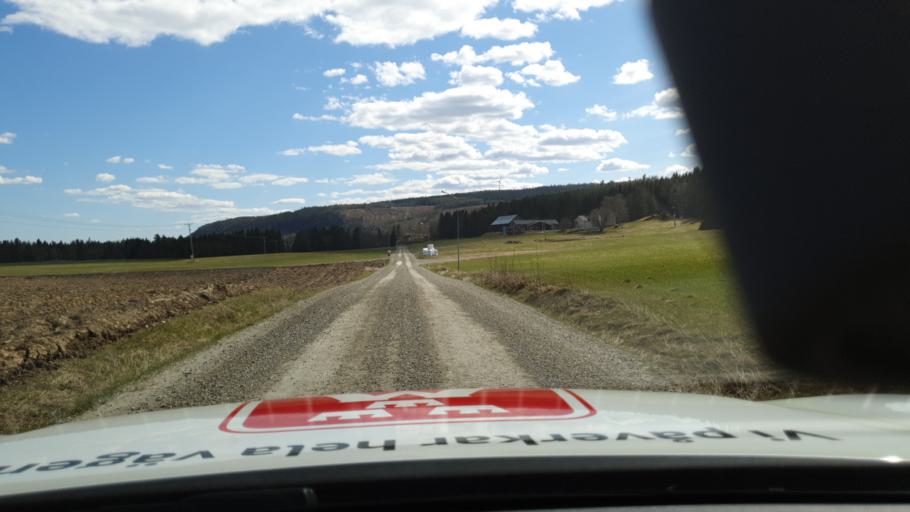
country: SE
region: Jaemtland
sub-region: Bergs Kommun
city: Hoverberg
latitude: 62.9530
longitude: 14.2653
